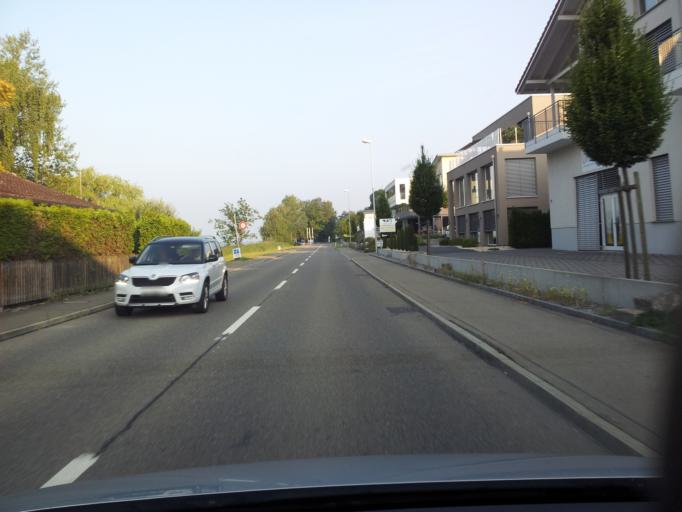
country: CH
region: Lucerne
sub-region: Sursee District
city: Eich
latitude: 47.1520
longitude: 8.1644
